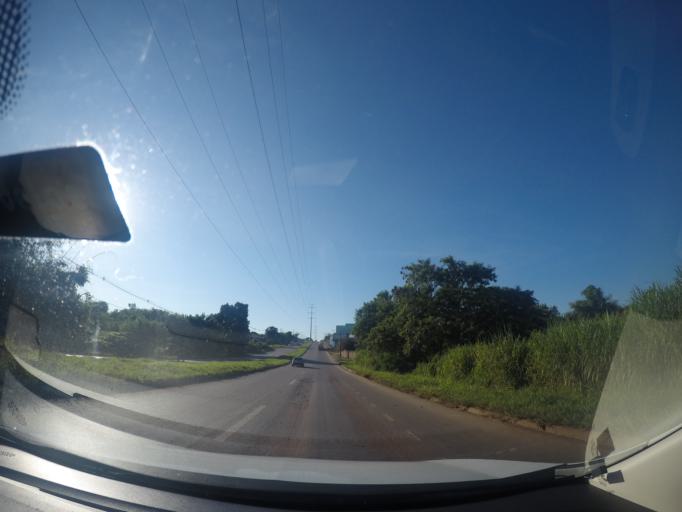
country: BR
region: Goias
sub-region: Aparecida De Goiania
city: Aparecida de Goiania
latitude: -16.7623
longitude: -49.3285
